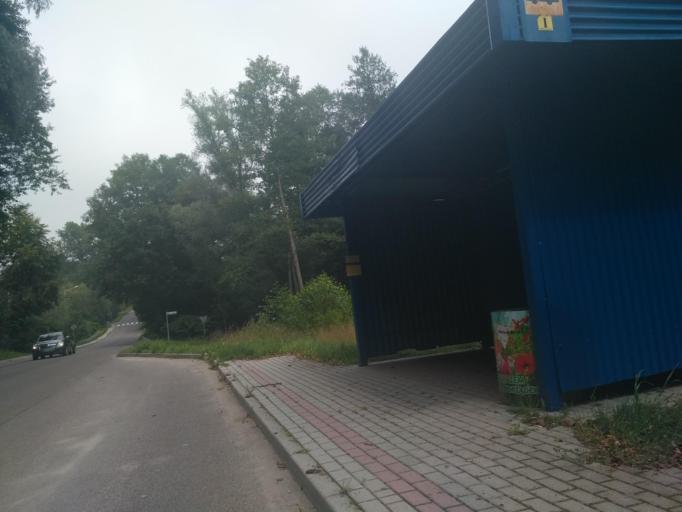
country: PL
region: Subcarpathian Voivodeship
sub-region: Powiat rzeszowski
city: Chmielnik
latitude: 49.9975
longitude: 22.1026
